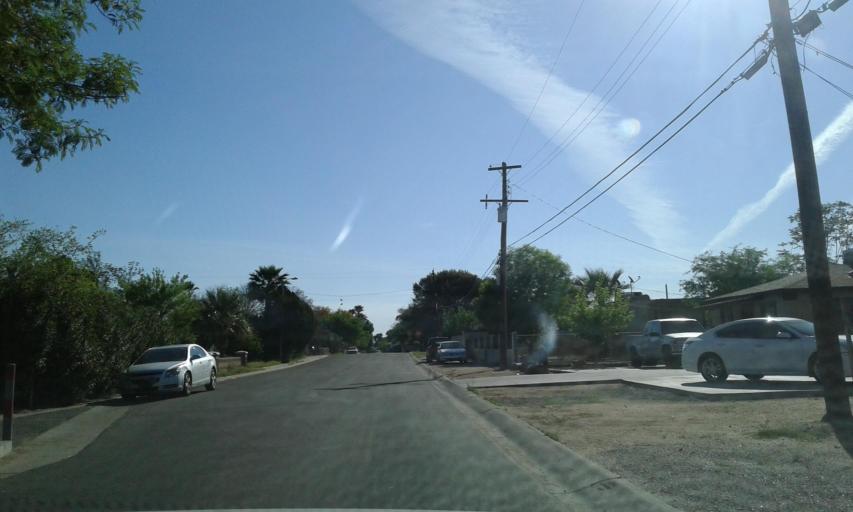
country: US
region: Arizona
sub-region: Maricopa County
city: Phoenix
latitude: 33.5032
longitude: -112.1075
